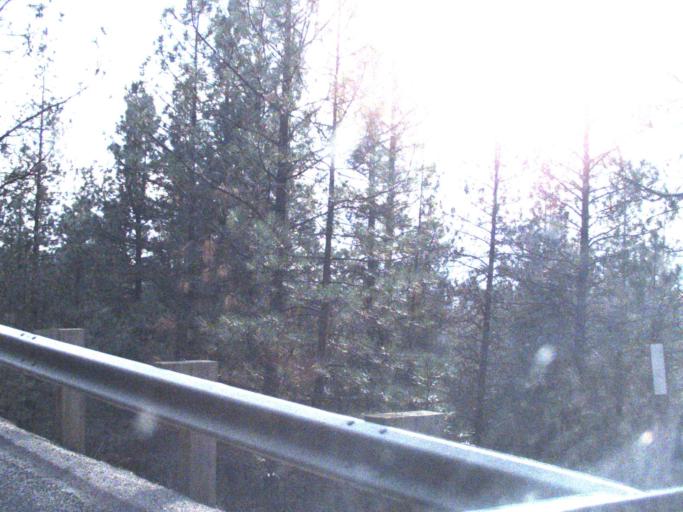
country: US
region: Washington
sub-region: Stevens County
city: Kettle Falls
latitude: 48.1847
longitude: -118.1709
